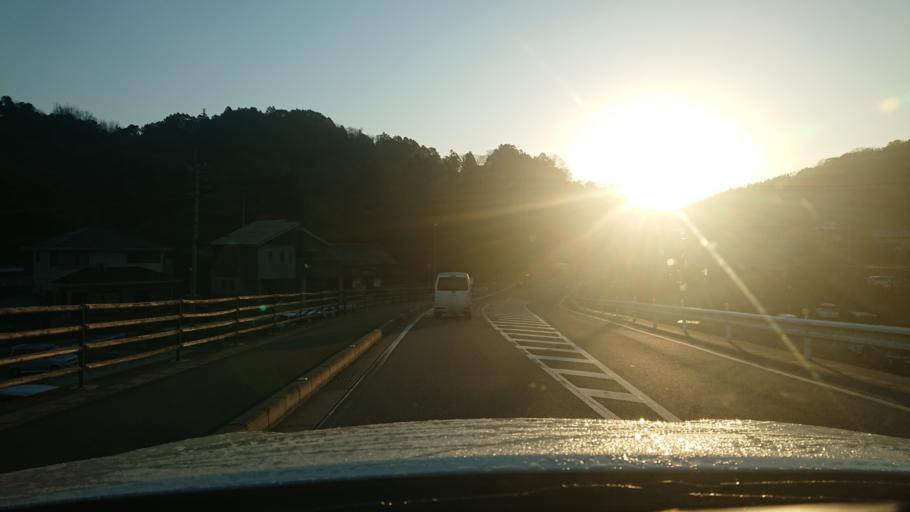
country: JP
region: Tokushima
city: Komatsushimacho
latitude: 33.9487
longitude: 134.5656
